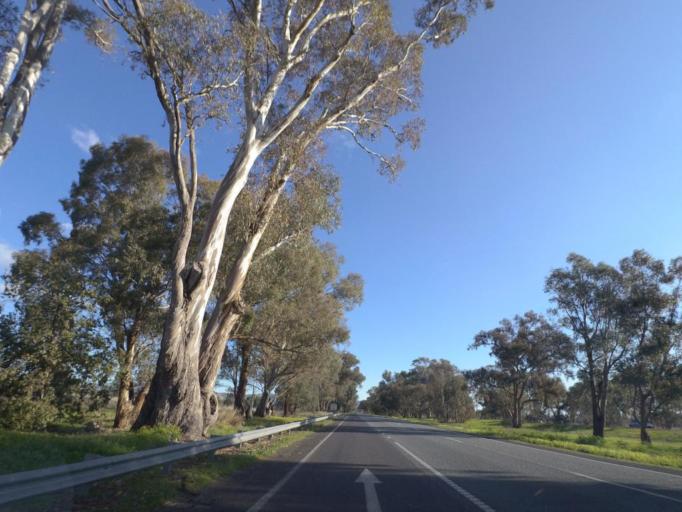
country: AU
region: Victoria
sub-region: Benalla
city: Benalla
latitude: -36.6970
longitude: 145.6567
